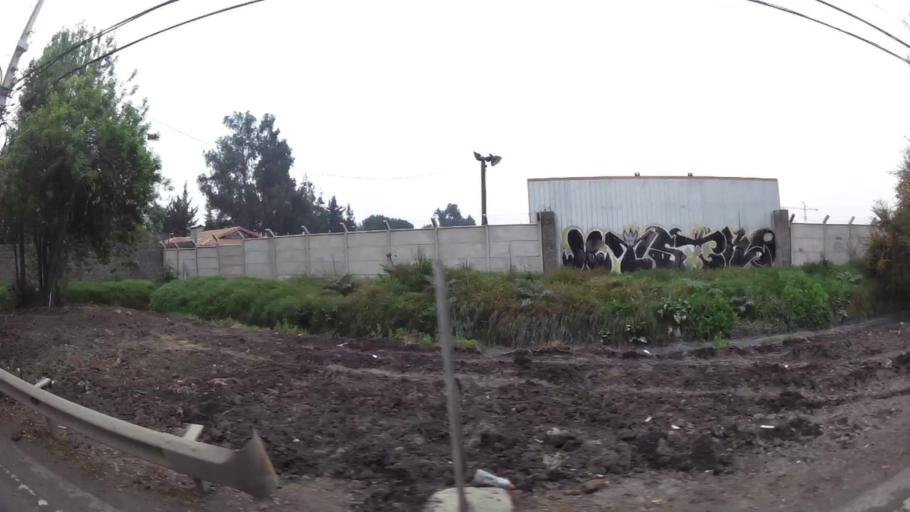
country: CL
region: Santiago Metropolitan
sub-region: Provincia de Chacabuco
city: Chicureo Abajo
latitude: -33.2587
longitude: -70.7621
